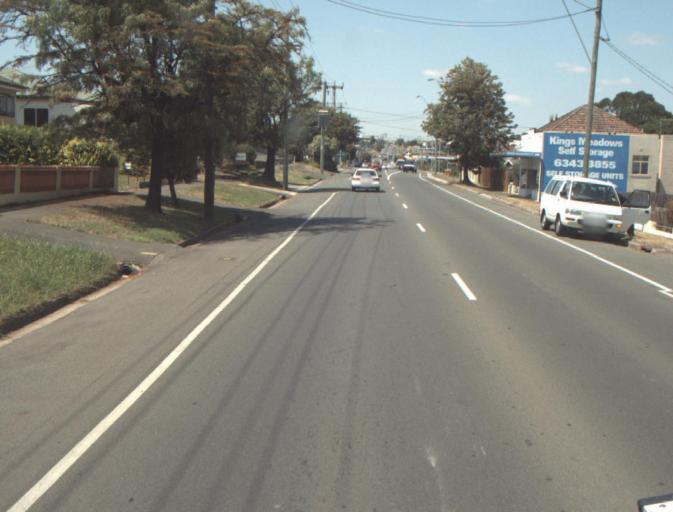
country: AU
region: Tasmania
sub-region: Launceston
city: Summerhill
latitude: -41.4738
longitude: 147.1637
